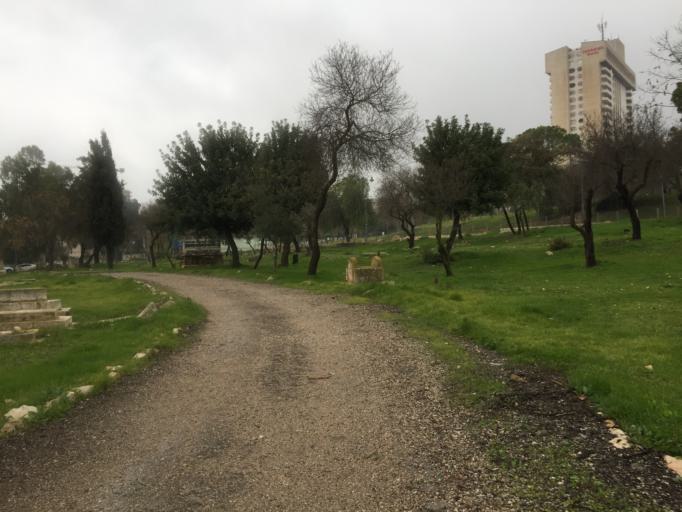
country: IL
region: Jerusalem
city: West Jerusalem
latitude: 31.7784
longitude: 35.2199
